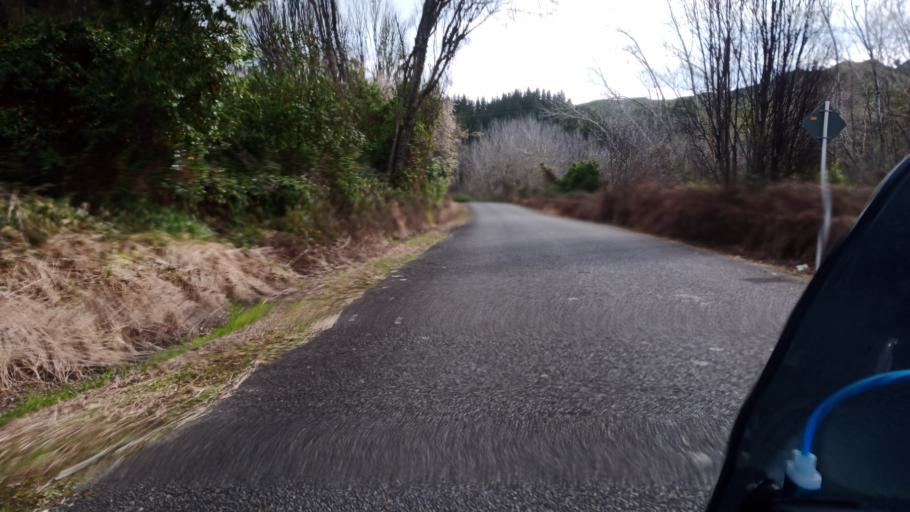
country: NZ
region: Hawke's Bay
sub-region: Wairoa District
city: Wairoa
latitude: -38.8261
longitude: 177.5126
